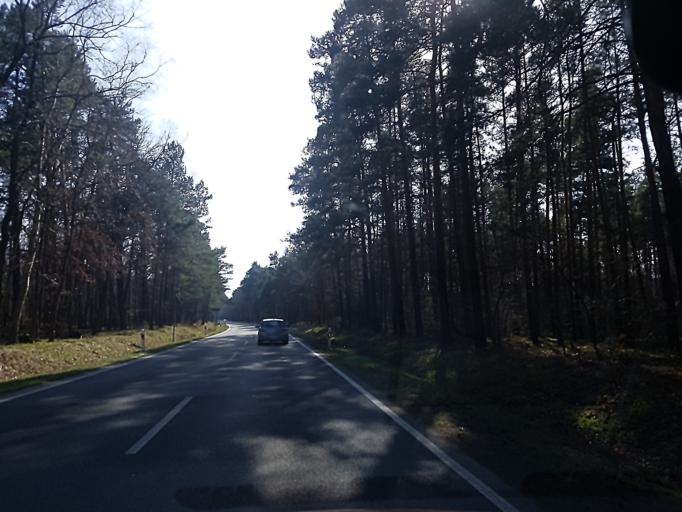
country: DE
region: Brandenburg
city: Calau
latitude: 51.7202
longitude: 13.9262
